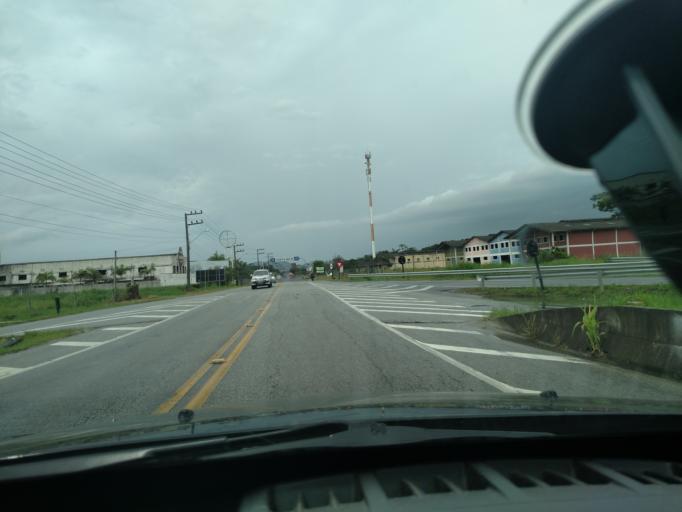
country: BR
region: Santa Catarina
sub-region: Porto Belo
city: Porto Belo
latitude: -27.1632
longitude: -48.6121
